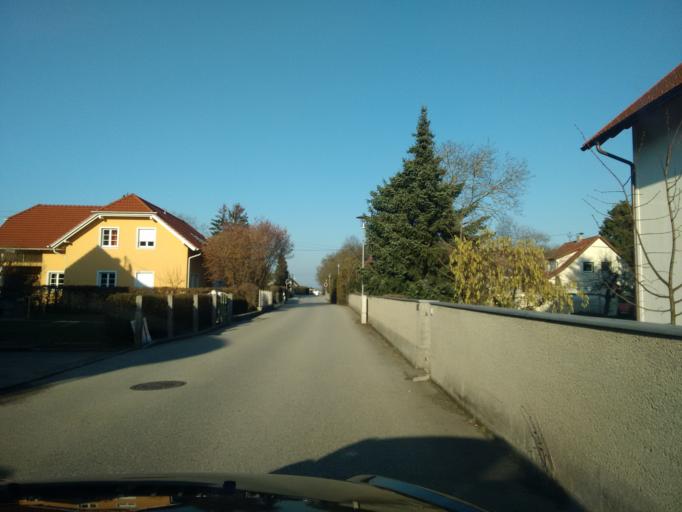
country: AT
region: Upper Austria
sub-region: Wels-Land
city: Marchtrenk
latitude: 48.1986
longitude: 14.1020
